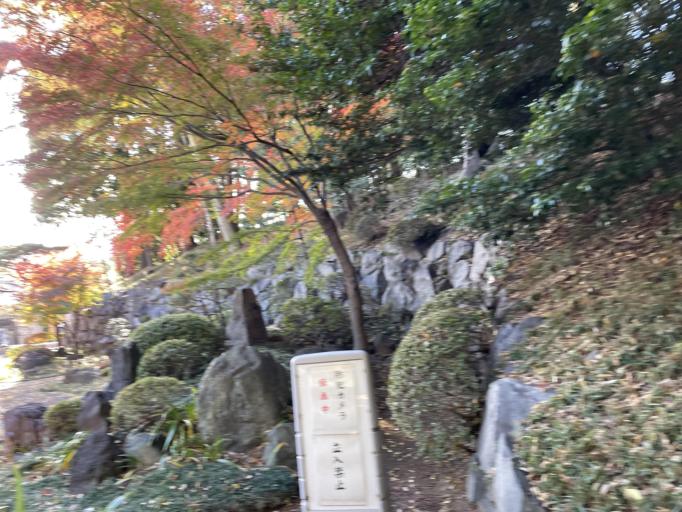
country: JP
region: Saitama
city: Wako
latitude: 35.7919
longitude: 139.6343
